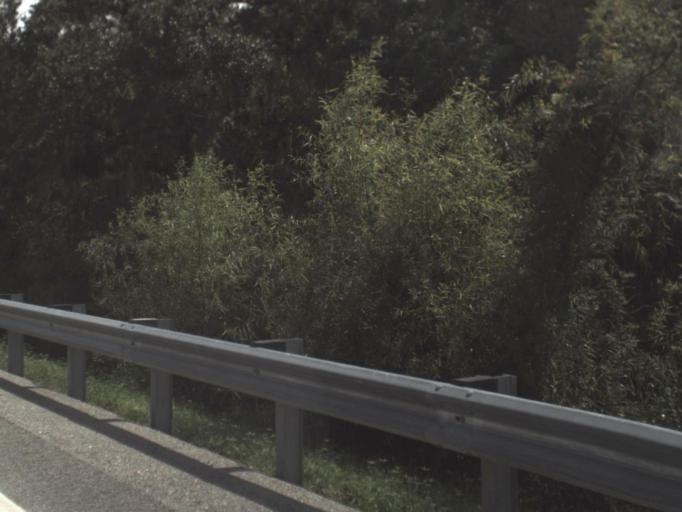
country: US
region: Florida
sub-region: Sarasota County
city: Lake Sarasota
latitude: 27.2321
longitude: -82.3085
